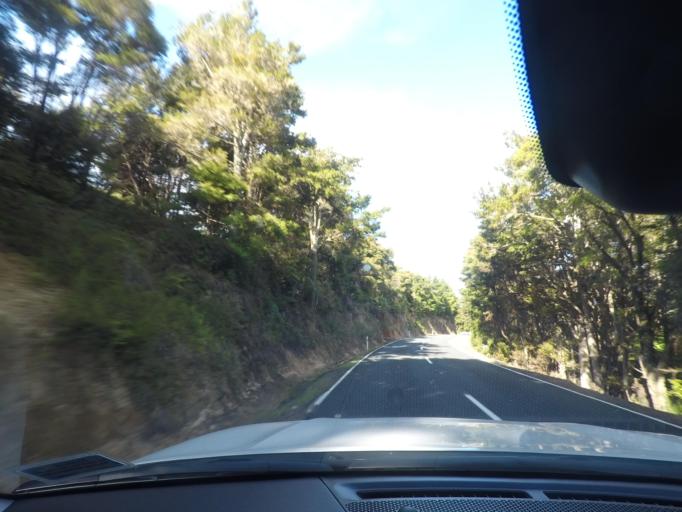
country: NZ
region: Northland
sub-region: Whangarei
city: Ngunguru
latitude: -35.6667
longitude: 174.4722
